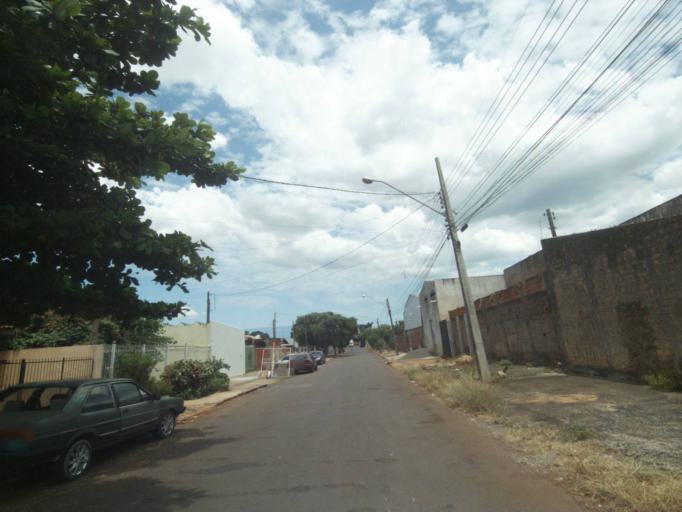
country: BR
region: Parana
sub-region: Londrina
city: Londrina
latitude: -23.3057
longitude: -51.2216
